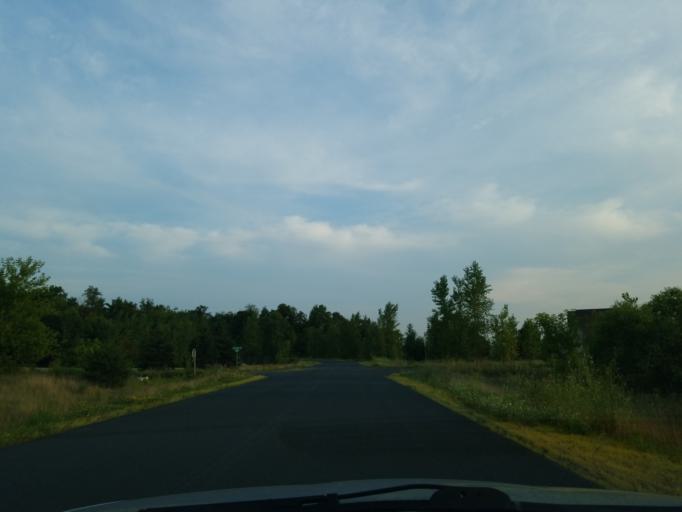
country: US
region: Minnesota
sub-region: Washington County
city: Stillwater
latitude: 45.0697
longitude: -92.7754
